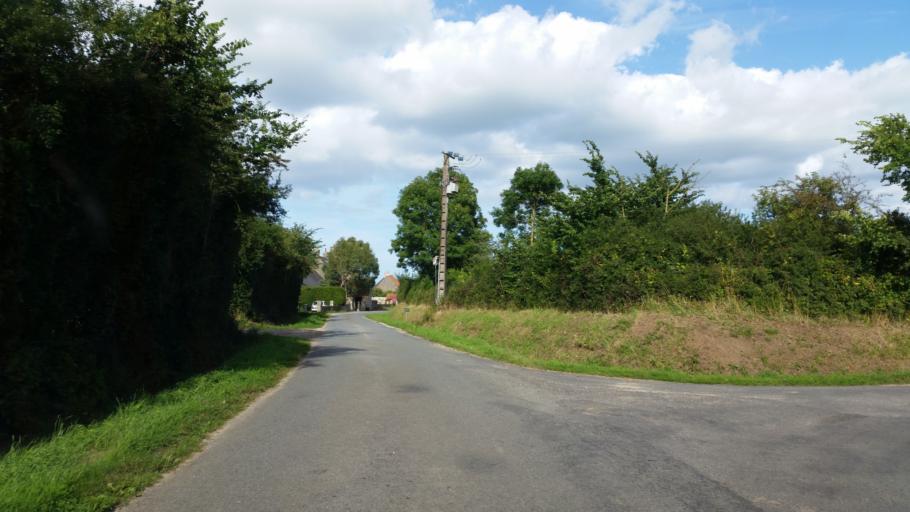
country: FR
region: Lower Normandy
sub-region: Departement de la Manche
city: Sainte-Mere-Eglise
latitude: 49.4537
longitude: -1.2859
